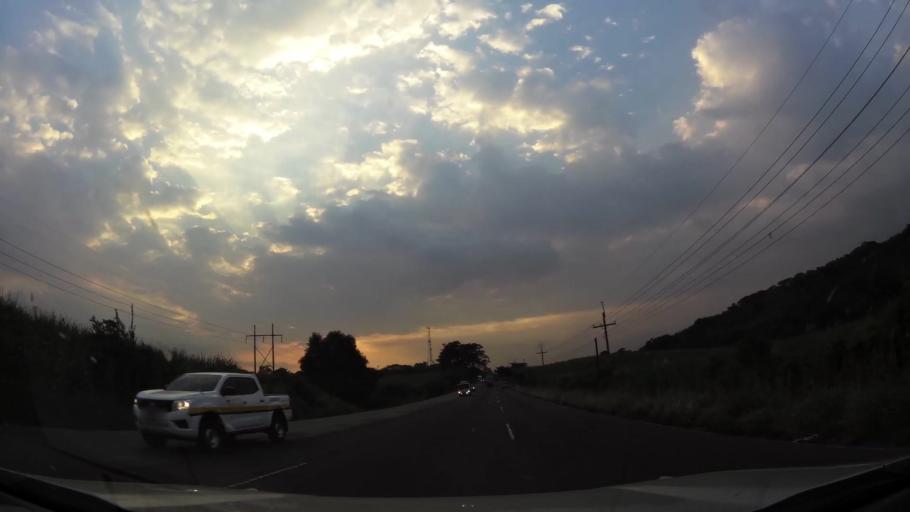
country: GT
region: Escuintla
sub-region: Municipio de Masagua
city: Masagua
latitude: 14.2673
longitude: -90.8813
